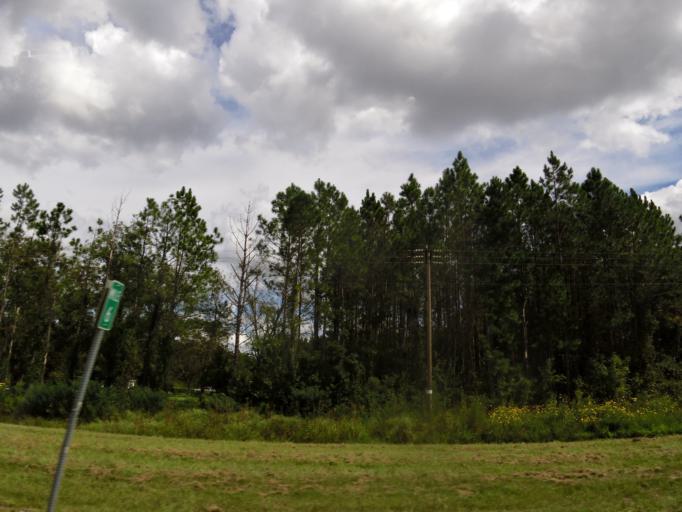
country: US
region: Georgia
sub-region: Brantley County
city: Nahunta
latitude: 31.1483
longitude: -81.9914
